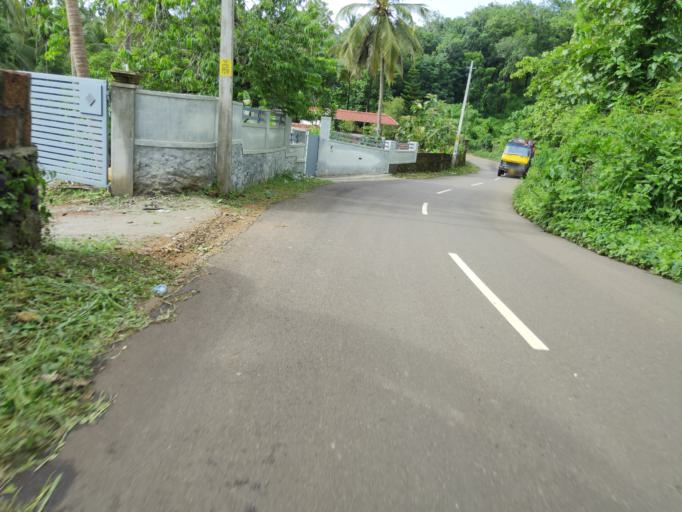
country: IN
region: Kerala
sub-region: Malappuram
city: Manjeri
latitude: 11.1393
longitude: 76.1318
